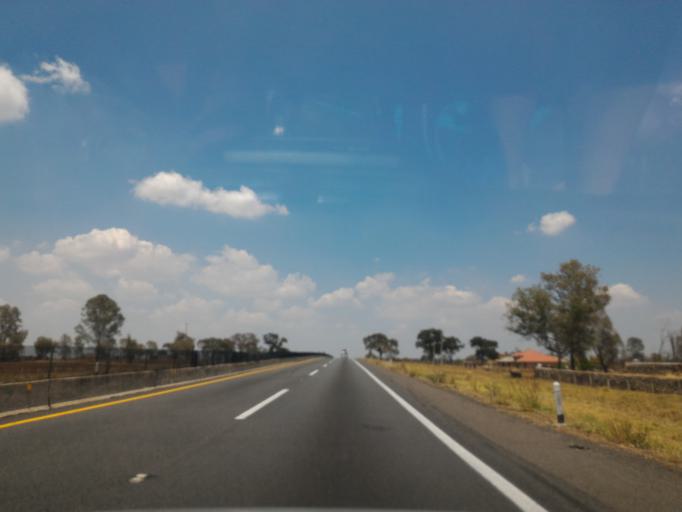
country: MX
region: Jalisco
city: Tepatitlan de Morelos
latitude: 20.8725
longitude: -102.7473
